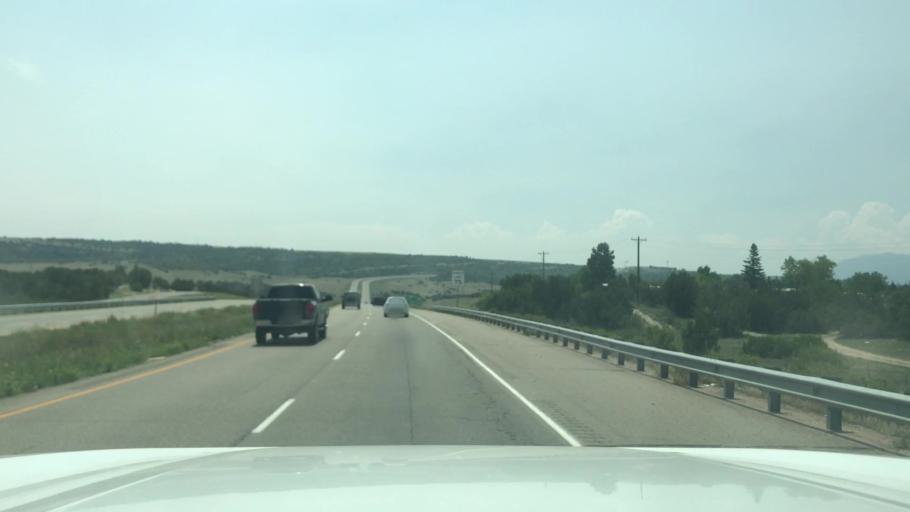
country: US
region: Colorado
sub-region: Pueblo County
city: Colorado City
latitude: 37.9564
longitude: -104.8004
